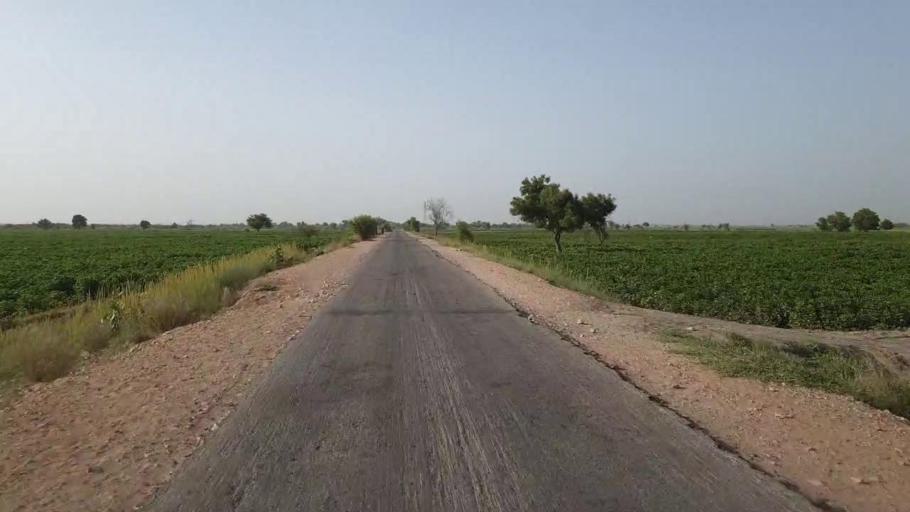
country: PK
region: Sindh
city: Jam Sahib
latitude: 26.4717
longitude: 68.8595
